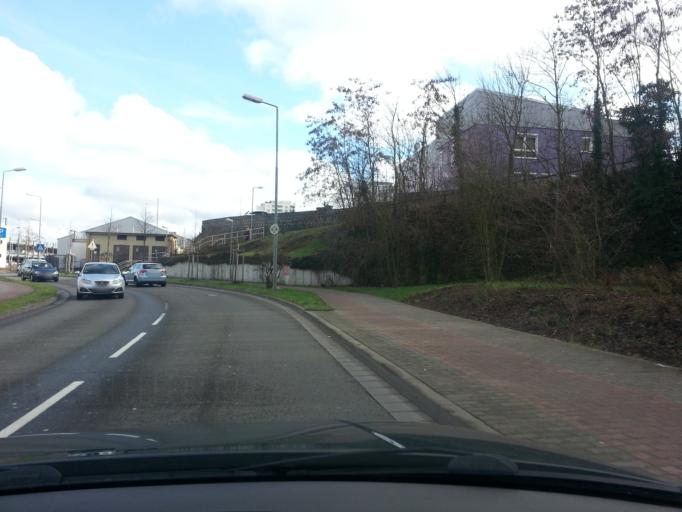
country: DE
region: Rheinland-Pfalz
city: Kaiserslautern
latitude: 49.4348
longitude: 7.7682
